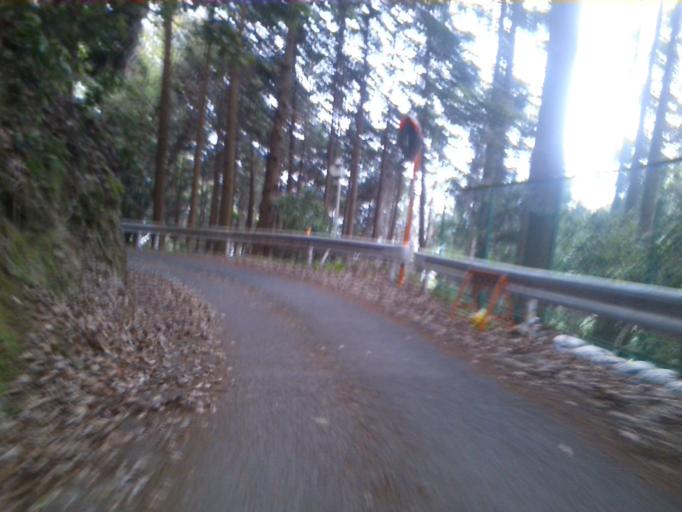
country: JP
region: Kyoto
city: Muko
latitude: 34.9493
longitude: 135.6401
